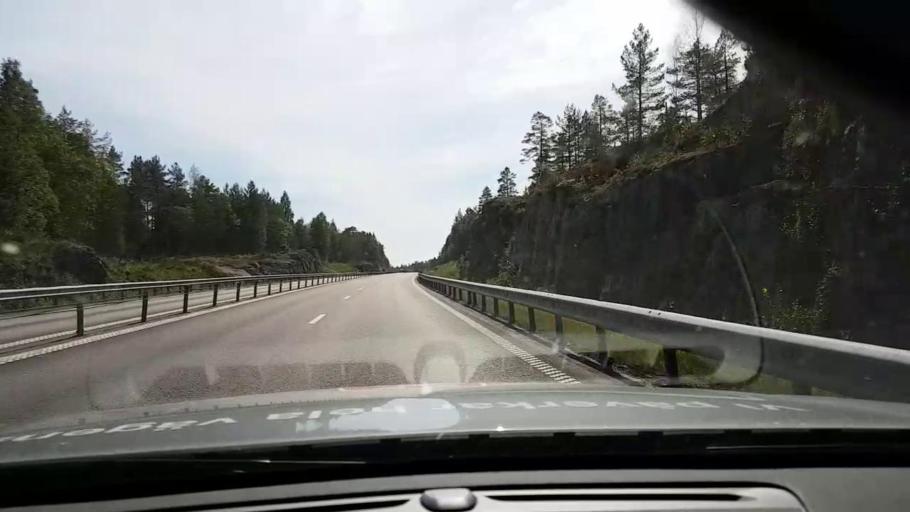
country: SE
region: Vaesternorrland
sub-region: OErnskoeldsviks Kommun
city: Husum
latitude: 63.3861
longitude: 19.1942
